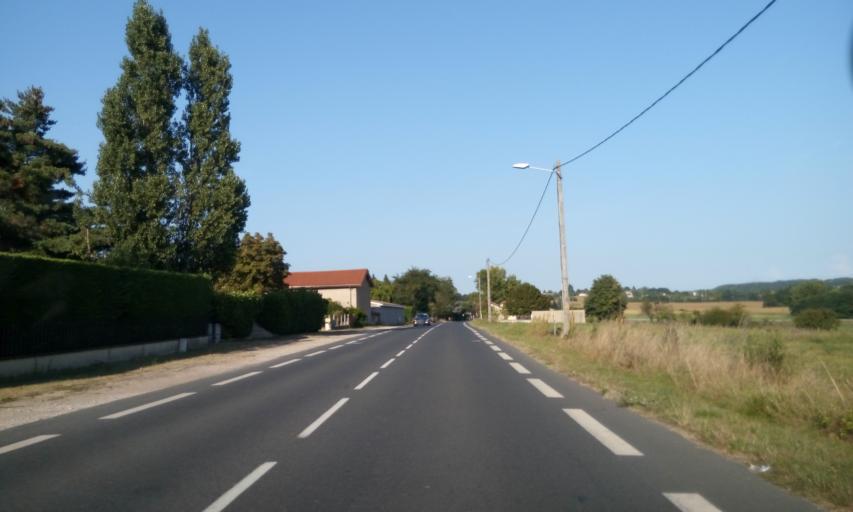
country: FR
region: Rhone-Alpes
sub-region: Departement de l'Ain
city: Trevoux
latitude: 45.9530
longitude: 4.7505
